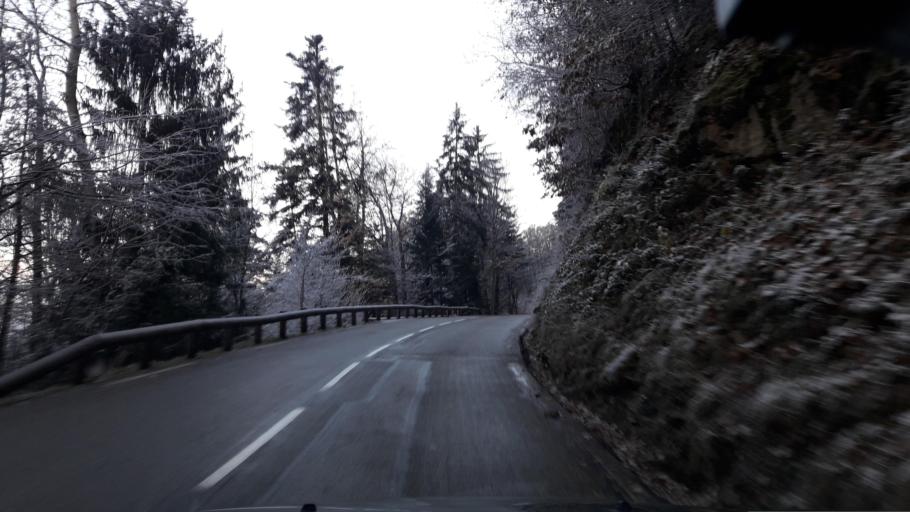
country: FR
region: Rhone-Alpes
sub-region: Departement de l'Isere
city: Allevard
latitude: 45.3878
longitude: 6.0903
